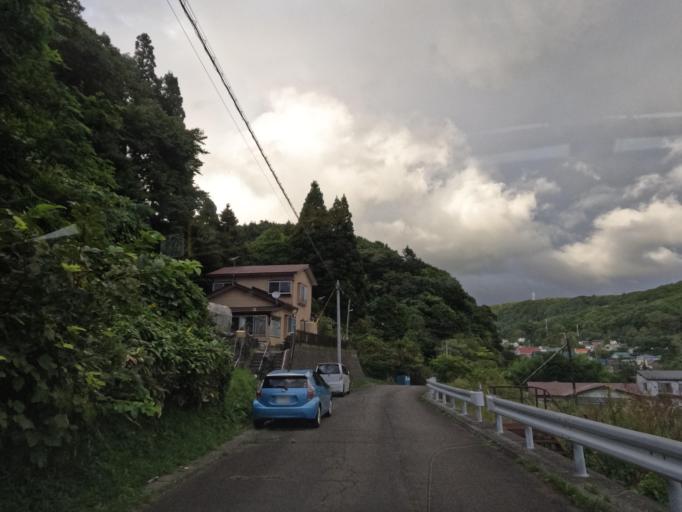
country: JP
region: Hokkaido
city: Muroran
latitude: 42.3709
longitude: 140.9533
